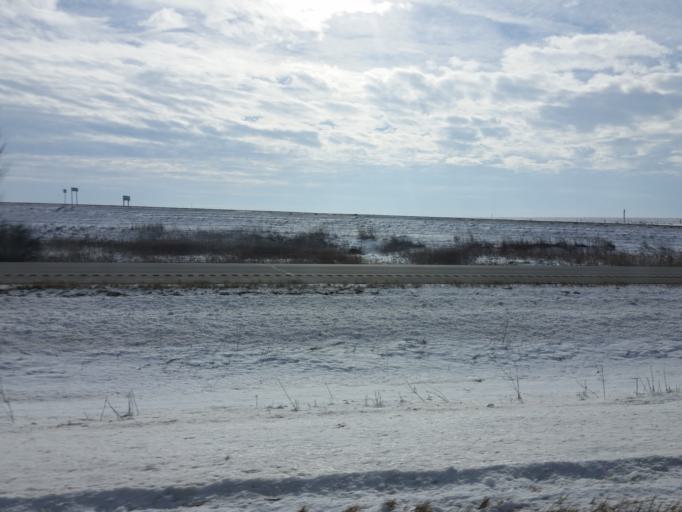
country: US
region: Iowa
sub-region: Buchanan County
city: Independence
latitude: 42.4618
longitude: -91.7549
